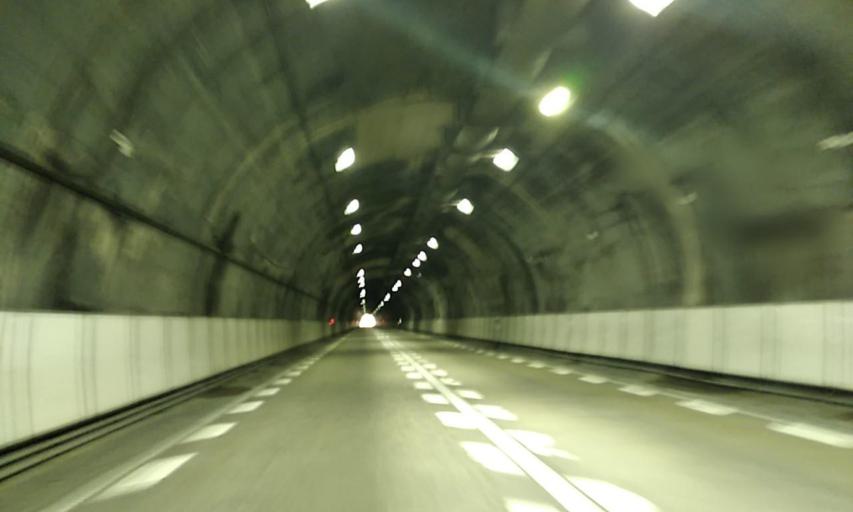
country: JP
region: Mie
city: Owase
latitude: 33.8922
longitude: 136.1107
